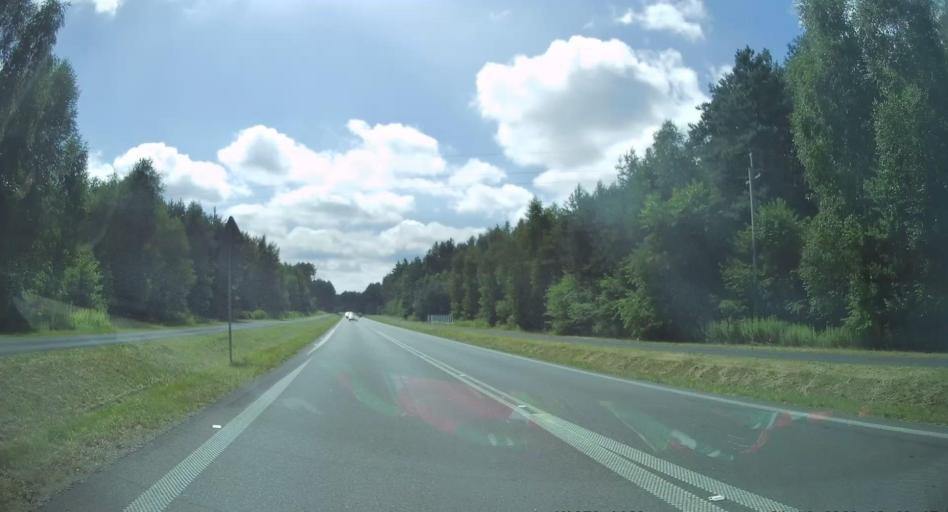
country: PL
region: Subcarpathian Voivodeship
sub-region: Powiat mielecki
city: Padew Narodowa
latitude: 50.3646
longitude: 21.4830
